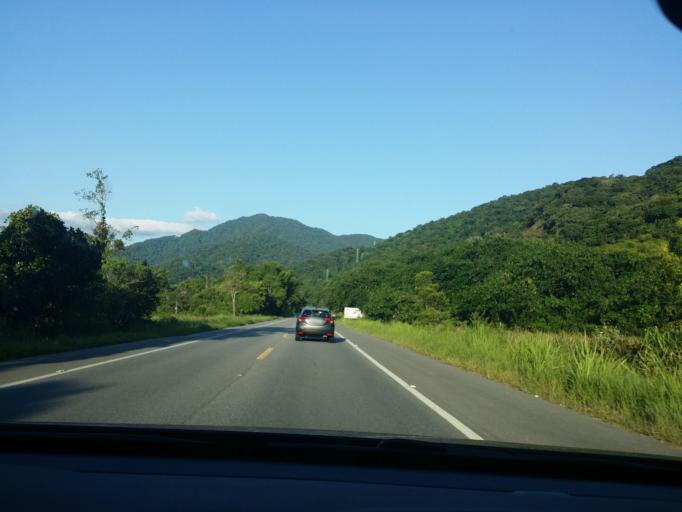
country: BR
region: Sao Paulo
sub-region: Sao Sebastiao
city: Sao Sebastiao
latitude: -23.7502
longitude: -45.7476
